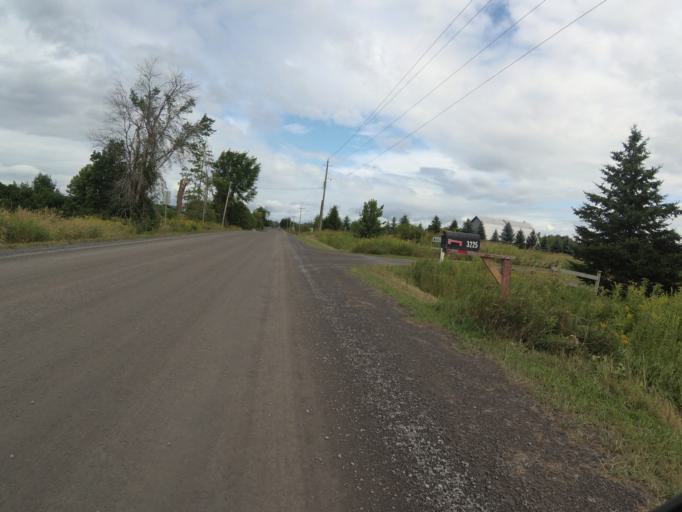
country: CA
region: Ontario
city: Clarence-Rockland
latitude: 45.4615
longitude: -75.2985
